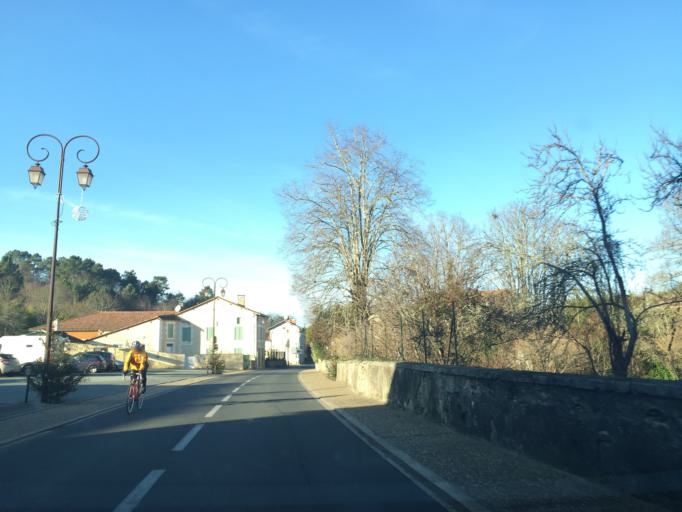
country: FR
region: Aquitaine
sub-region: Departement de la Dordogne
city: Neuvic
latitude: 45.1641
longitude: 0.3969
